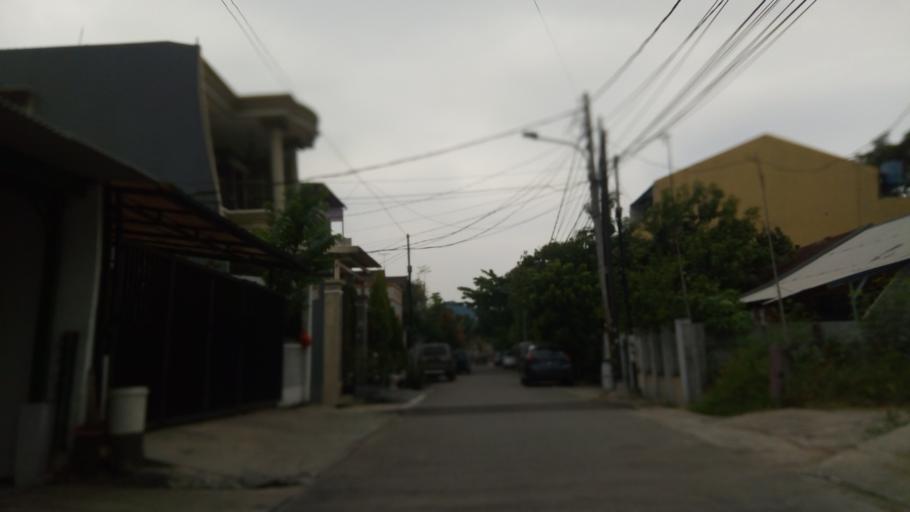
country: ID
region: Jakarta Raya
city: Jakarta
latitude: -6.1516
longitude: 106.8394
